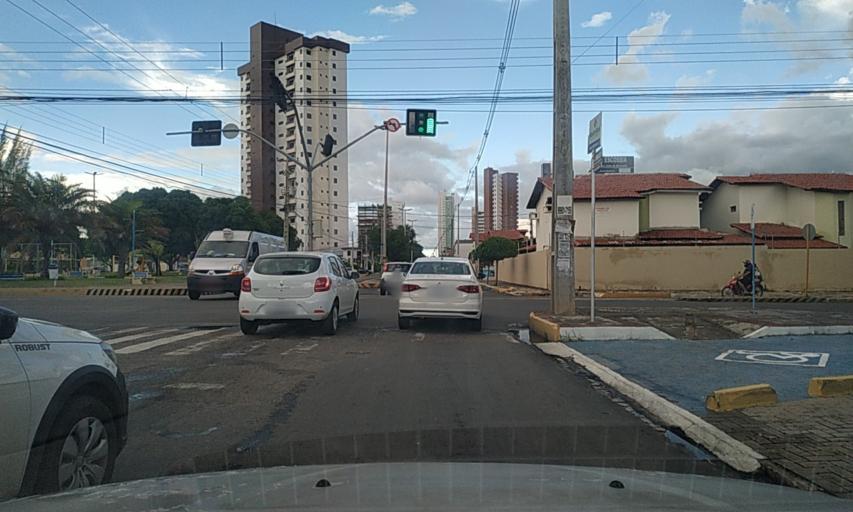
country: BR
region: Rio Grande do Norte
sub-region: Mossoro
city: Mossoro
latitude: -5.1815
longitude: -37.3616
